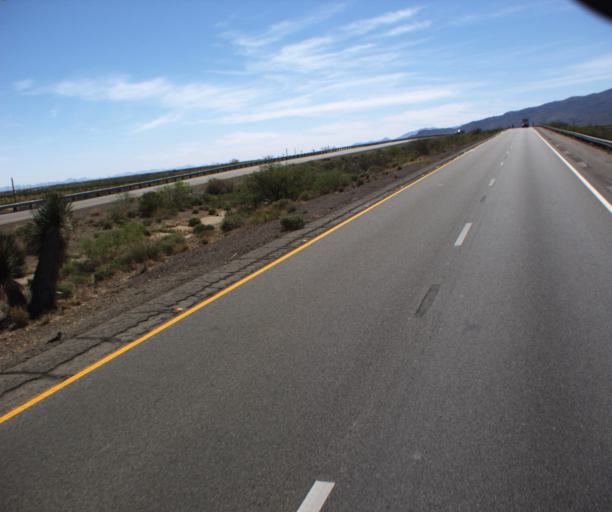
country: US
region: Arizona
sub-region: Cochise County
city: Willcox
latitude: 32.3557
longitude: -109.6114
